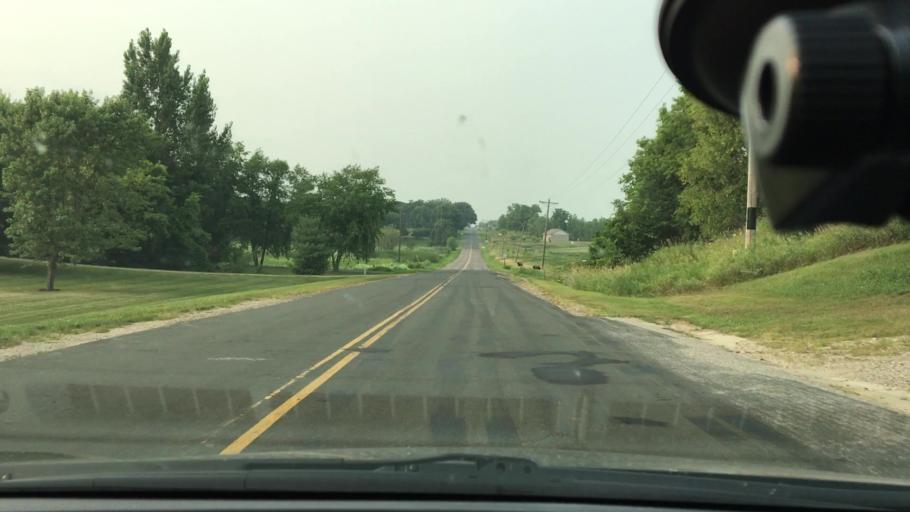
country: US
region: Minnesota
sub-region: Wright County
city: Albertville
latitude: 45.2767
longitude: -93.6841
